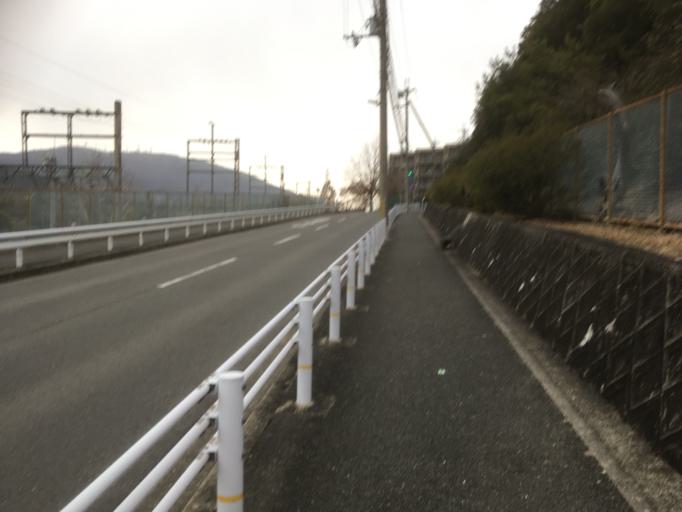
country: JP
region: Nara
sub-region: Ikoma-shi
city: Ikoma
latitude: 34.6525
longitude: 135.7091
